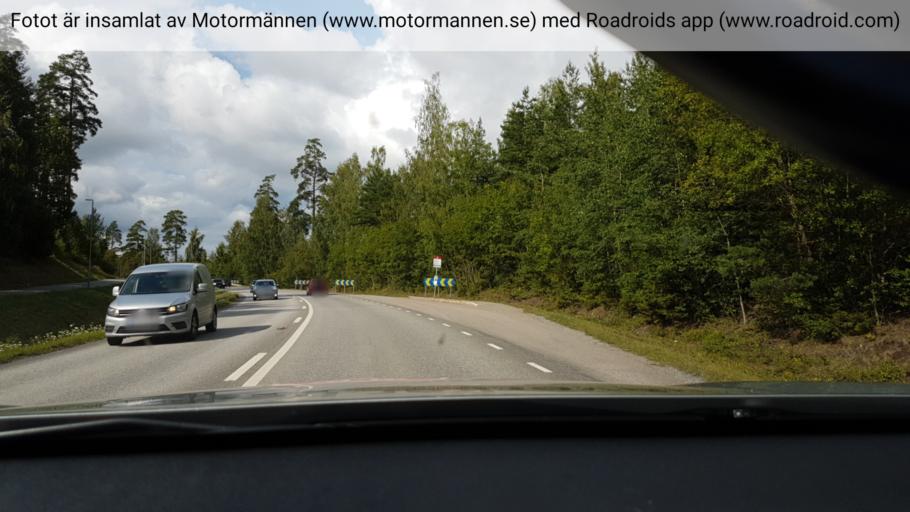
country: SE
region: Stockholm
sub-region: Ekero Kommun
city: Ekeroe
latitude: 59.3002
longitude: 17.8100
